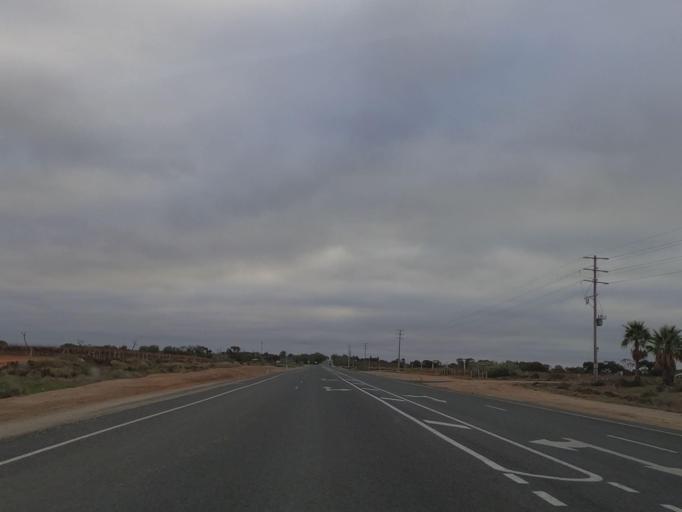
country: AU
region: Victoria
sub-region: Swan Hill
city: Swan Hill
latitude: -35.4716
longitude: 143.6683
